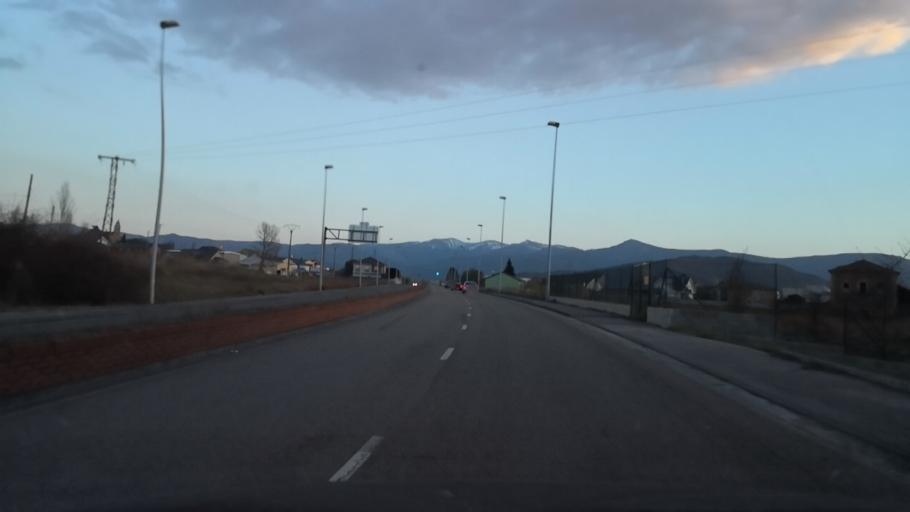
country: ES
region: Castille and Leon
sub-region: Provincia de Leon
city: Ponferrada
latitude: 42.5753
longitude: -6.6098
